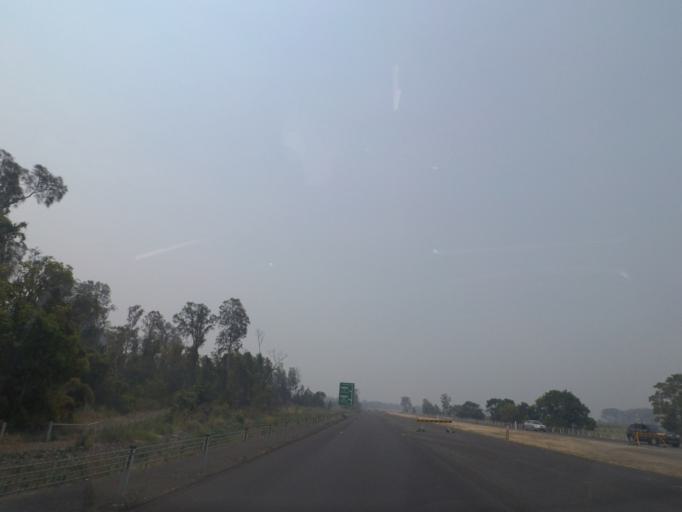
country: AU
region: New South Wales
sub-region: Ballina
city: Ballina
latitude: -28.8767
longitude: 153.4884
